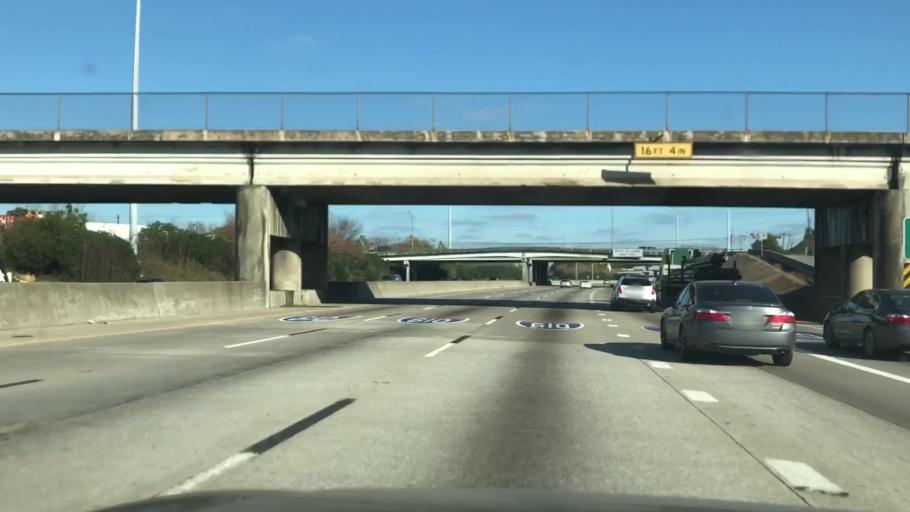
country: US
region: Texas
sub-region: Harris County
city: Jacinto City
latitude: 29.7680
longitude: -95.2653
